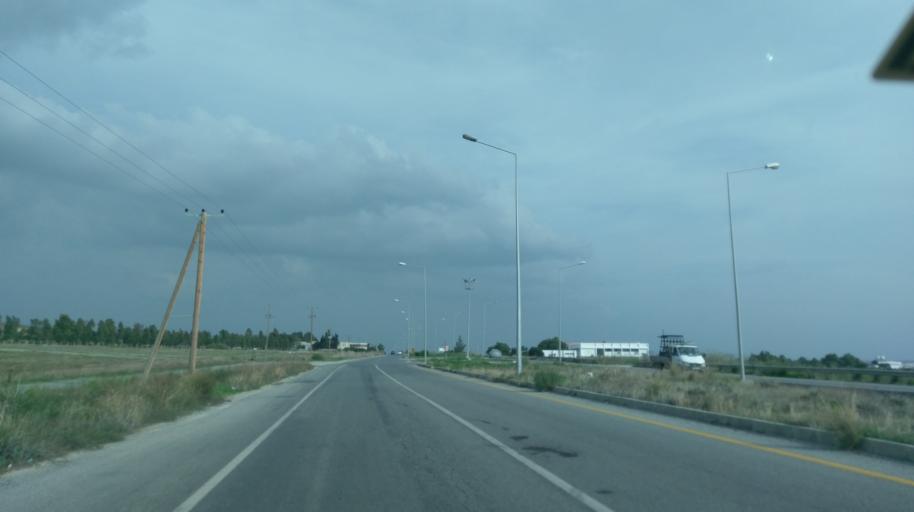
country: CY
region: Lefkosia
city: Mammari
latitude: 35.2122
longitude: 33.2486
